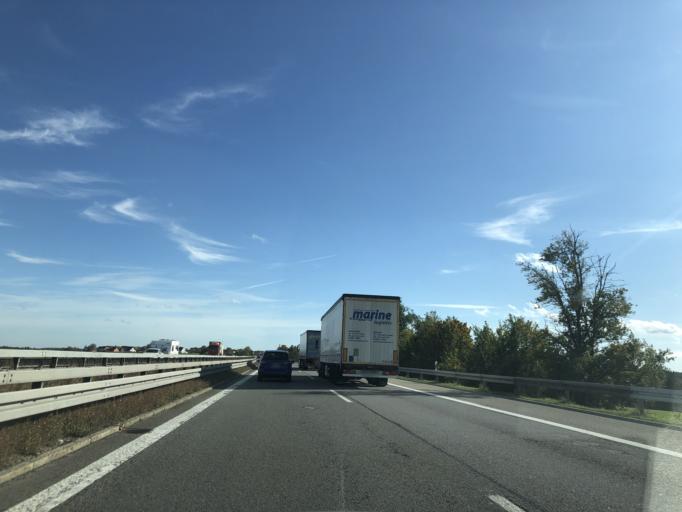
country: DE
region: Bavaria
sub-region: Upper Palatinate
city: Deuerling
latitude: 49.0563
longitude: 11.9237
